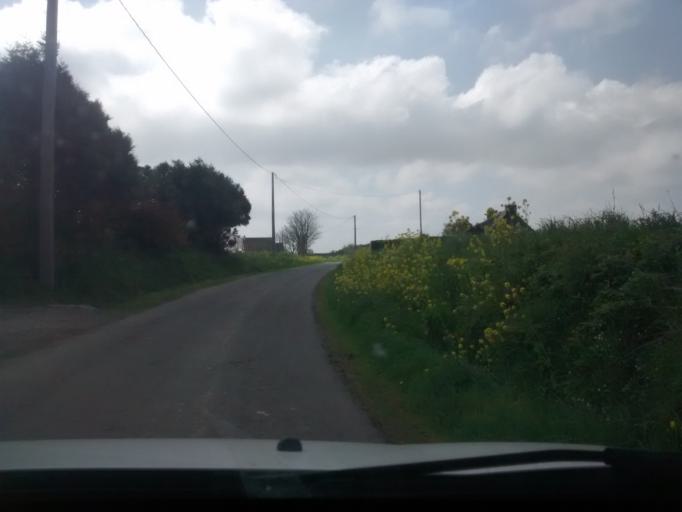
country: FR
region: Brittany
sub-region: Departement des Cotes-d'Armor
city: Penvenan
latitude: 48.8120
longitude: -3.3051
